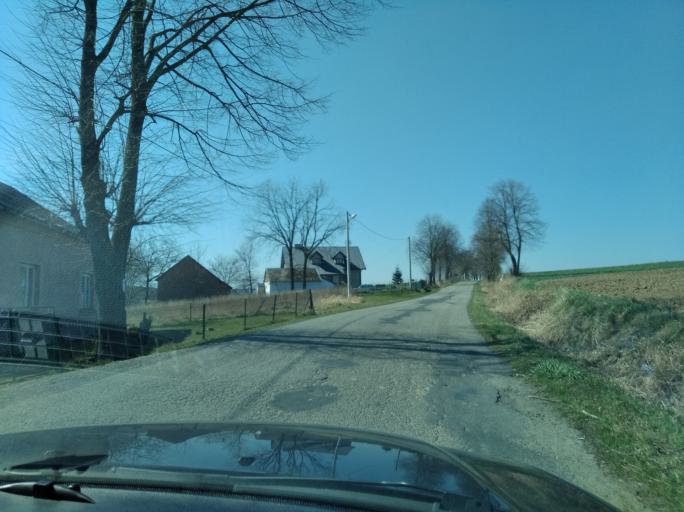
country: PL
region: Subcarpathian Voivodeship
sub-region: Powiat jaroslawski
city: Jodlowka
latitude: 49.9267
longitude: 22.4769
